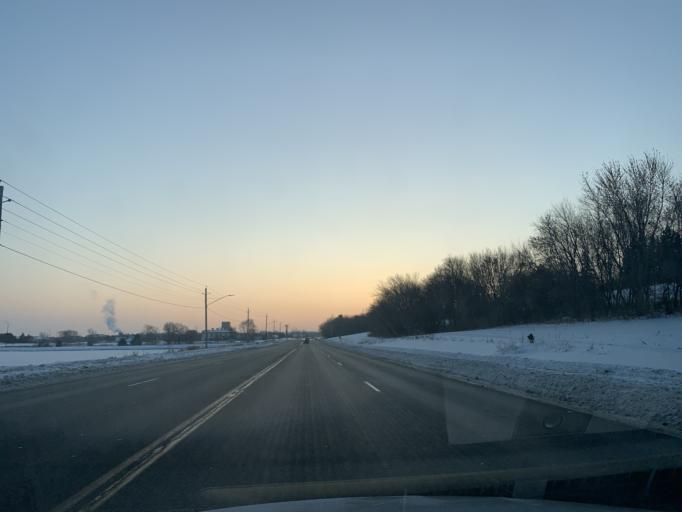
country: US
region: Minnesota
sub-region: Scott County
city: Shakopee
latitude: 44.7859
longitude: -93.4885
